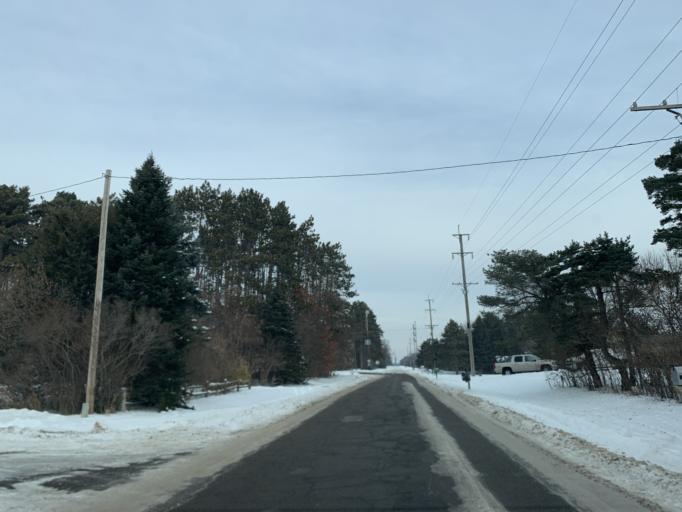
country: US
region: Minnesota
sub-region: Washington County
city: Forest Lake
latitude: 45.2851
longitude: -93.0090
